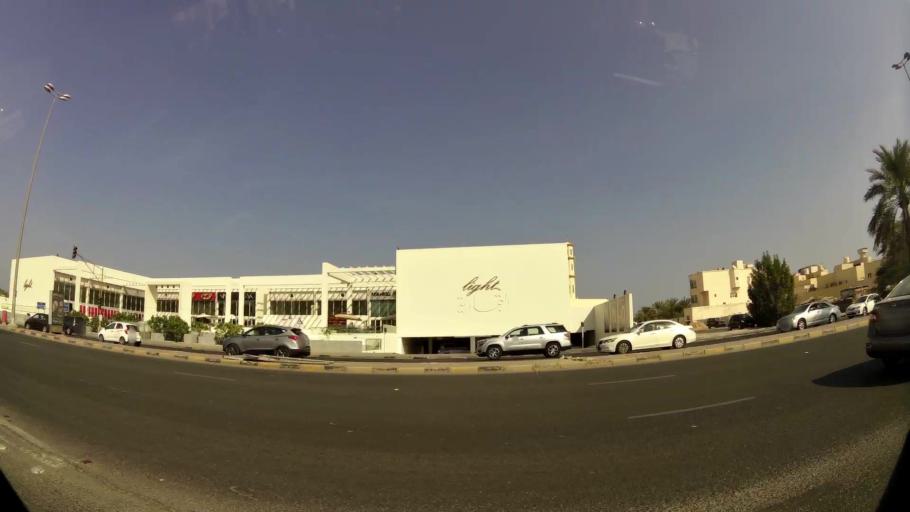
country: KW
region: Al Ahmadi
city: Al Mahbulah
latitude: 29.1375
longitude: 48.1300
